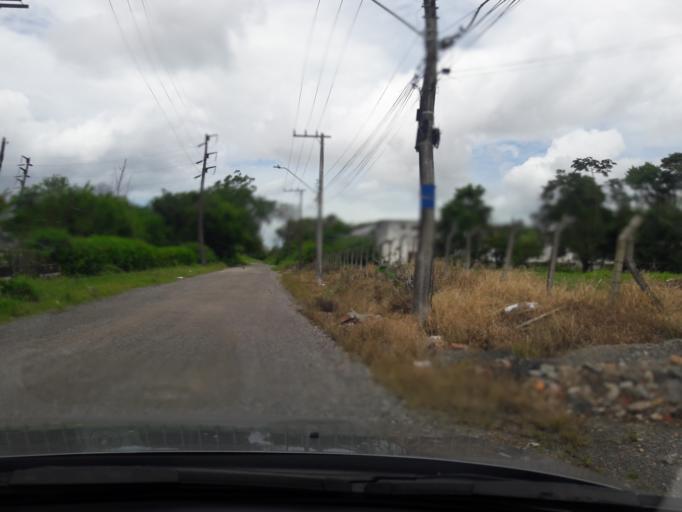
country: BR
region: Santa Catarina
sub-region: Joinville
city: Joinville
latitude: -26.3187
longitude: -48.8363
